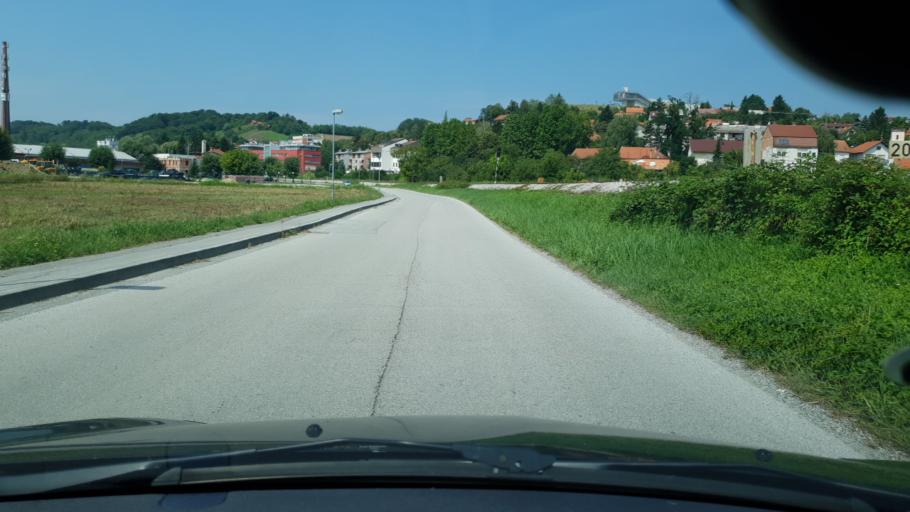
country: HR
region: Krapinsko-Zagorska
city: Zabok
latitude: 46.0259
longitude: 15.9114
